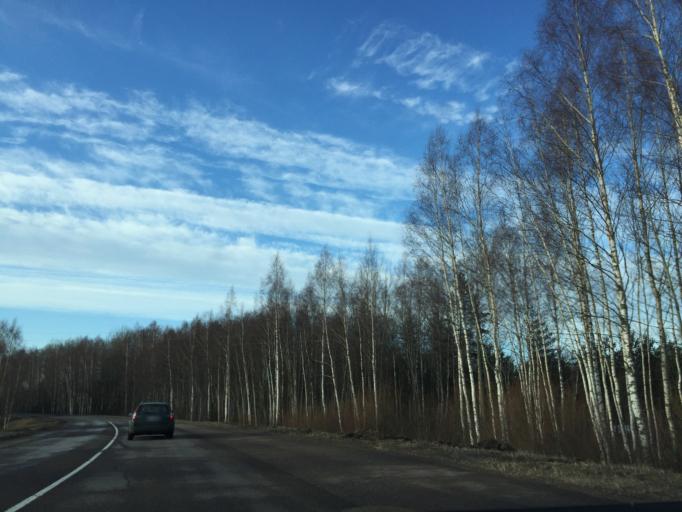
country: LV
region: Kekava
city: Balozi
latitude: 56.7765
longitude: 24.1106
